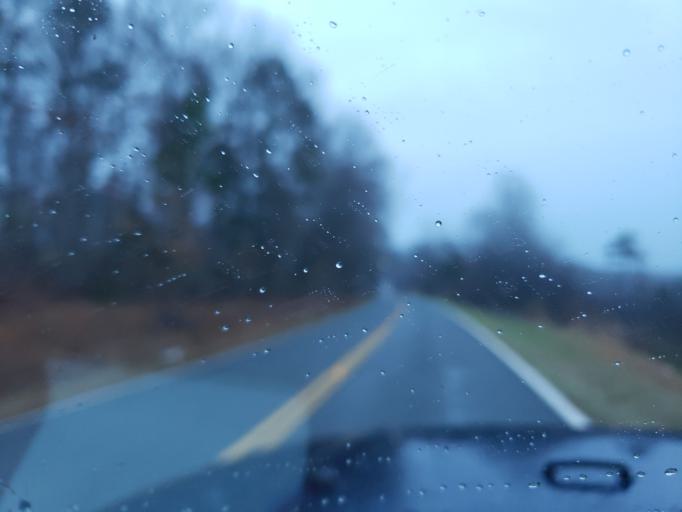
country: US
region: South Carolina
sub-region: Cherokee County
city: Blacksburg
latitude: 35.1416
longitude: -81.4478
